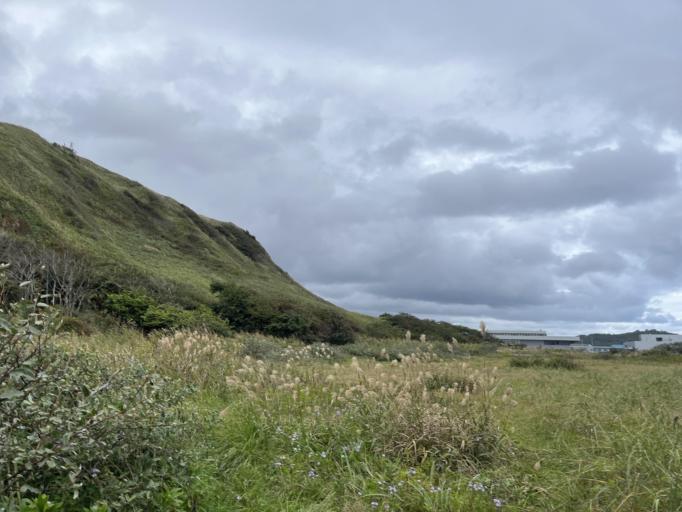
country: JP
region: Hokkaido
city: Muroran
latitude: 42.3311
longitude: 141.0199
